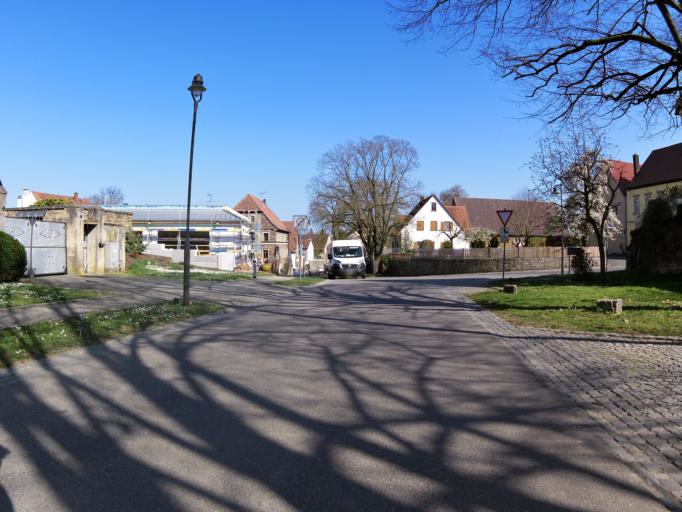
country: DE
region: Bavaria
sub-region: Regierungsbezirk Unterfranken
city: Prosselsheim
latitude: 49.8231
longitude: 10.1058
